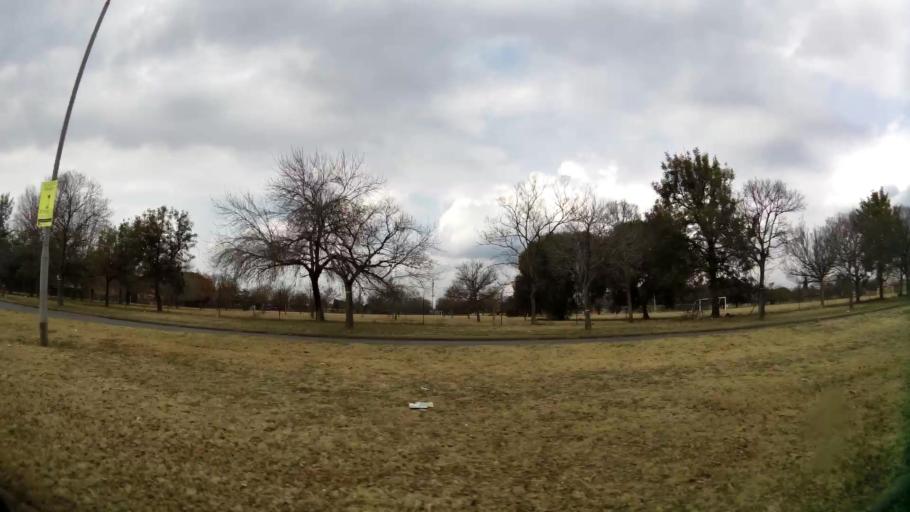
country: ZA
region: Gauteng
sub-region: Sedibeng District Municipality
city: Vanderbijlpark
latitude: -26.7148
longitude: 27.8235
